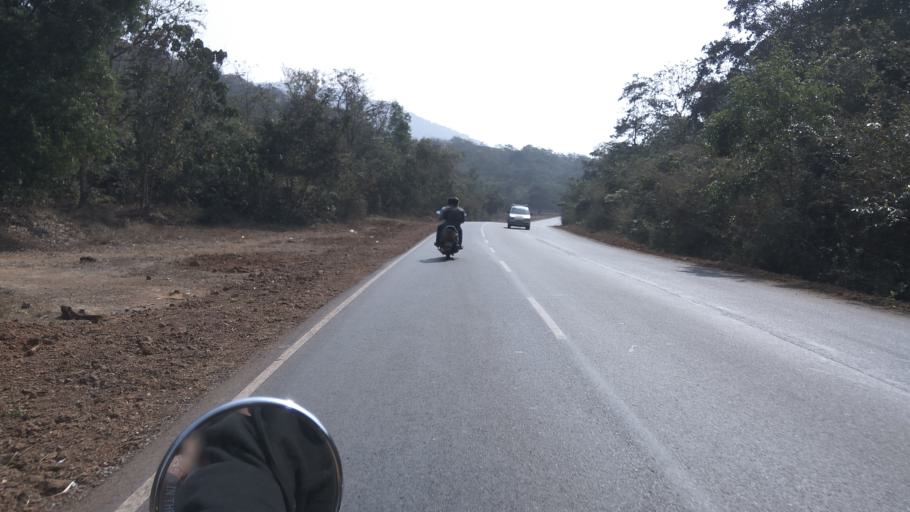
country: IN
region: Goa
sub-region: North Goa
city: Palle
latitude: 15.3860
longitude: 74.1366
